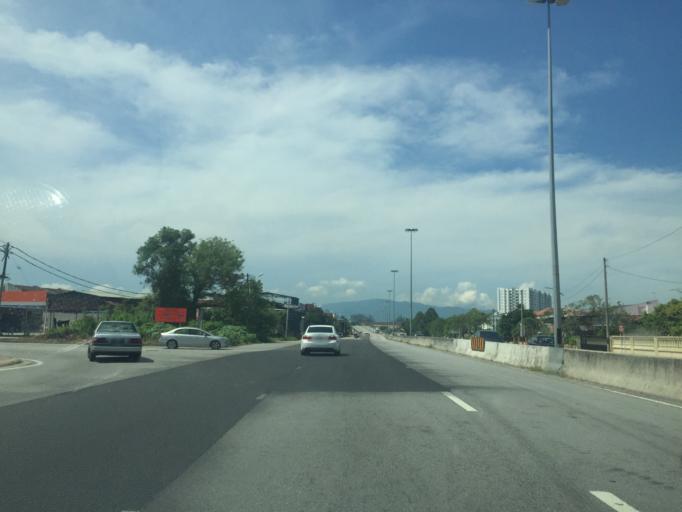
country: MY
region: Penang
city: Permatang Kuching
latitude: 5.4438
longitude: 100.3875
